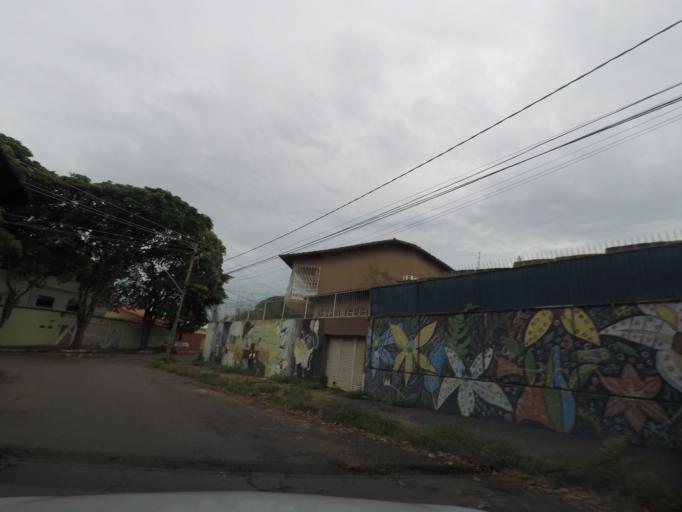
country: BR
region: Goias
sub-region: Goiania
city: Goiania
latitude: -16.6954
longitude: -49.2487
